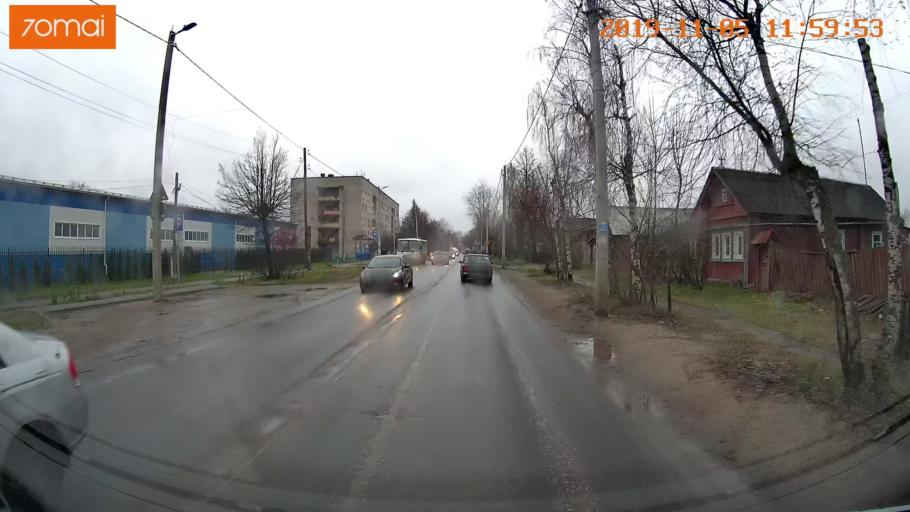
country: RU
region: Ivanovo
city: Kokhma
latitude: 56.9772
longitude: 41.0496
